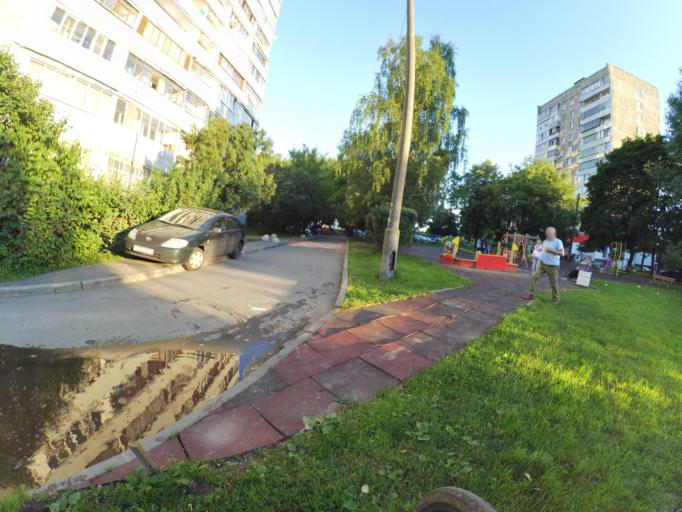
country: RU
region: Moscow
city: Strogino
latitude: 55.8279
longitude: 37.4256
